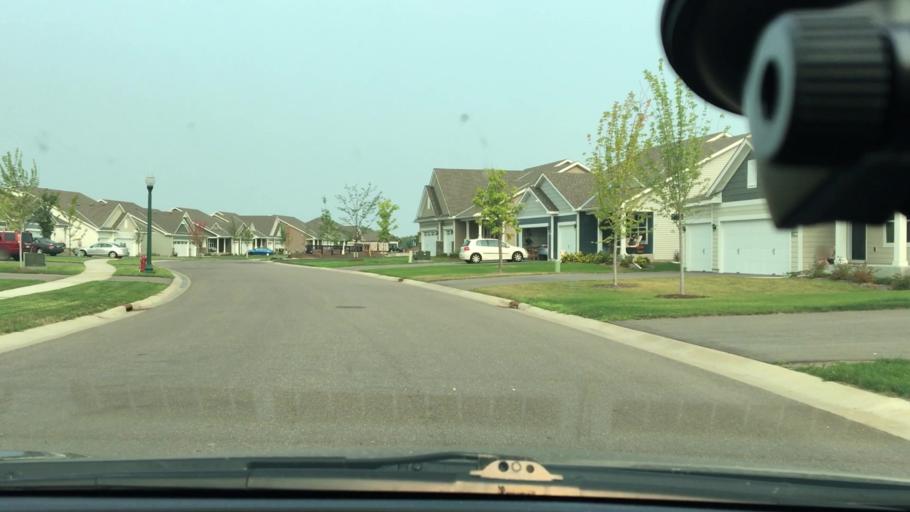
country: US
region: Minnesota
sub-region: Hennepin County
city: Champlin
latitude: 45.1982
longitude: -93.4389
